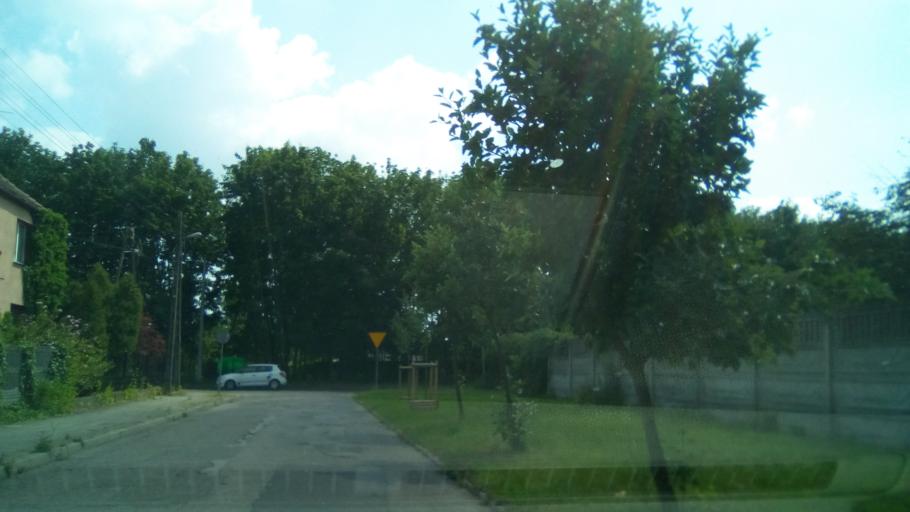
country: PL
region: Greater Poland Voivodeship
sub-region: Powiat gnieznienski
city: Gniezno
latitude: 52.5326
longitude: 17.6141
